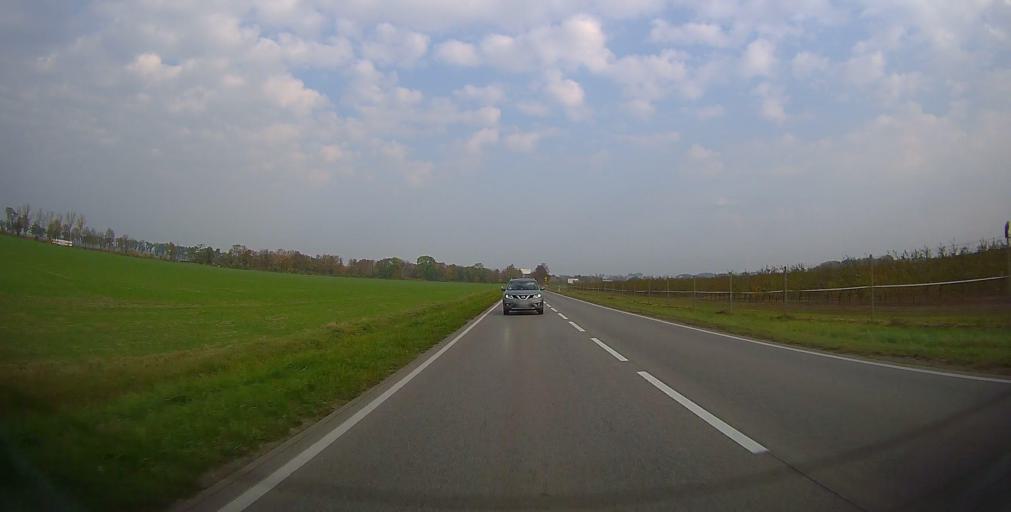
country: PL
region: Masovian Voivodeship
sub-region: Powiat grojecki
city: Belsk Duzy
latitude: 51.8050
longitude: 20.7916
